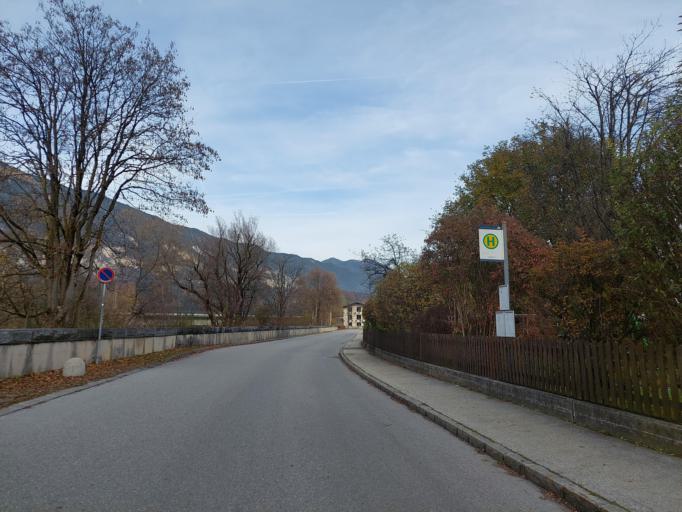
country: AT
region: Tyrol
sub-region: Politischer Bezirk Kufstein
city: Rattenberg
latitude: 47.4417
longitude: 11.8947
